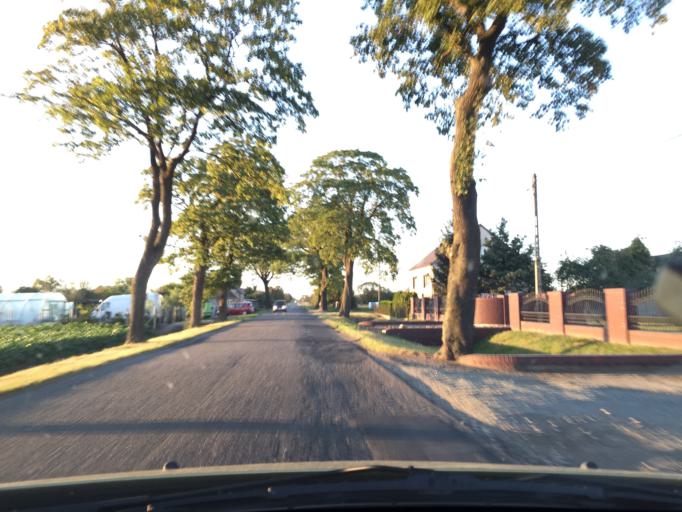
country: PL
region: Greater Poland Voivodeship
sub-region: Powiat pleszewski
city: Dobrzyca
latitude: 51.8216
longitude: 17.6207
